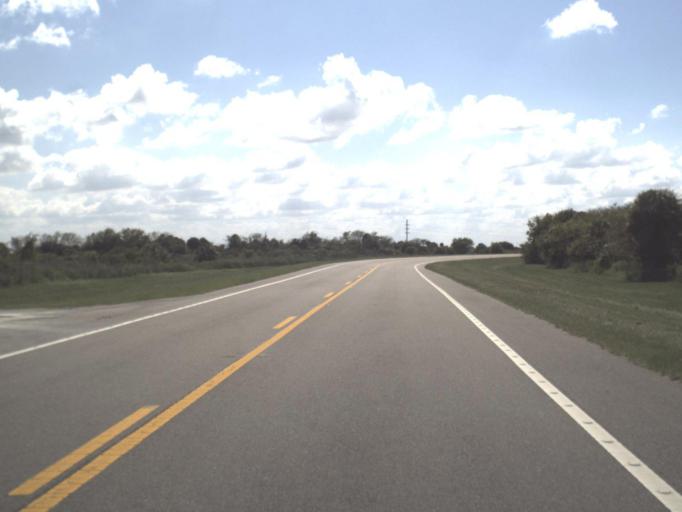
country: US
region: Florida
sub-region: Glades County
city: Moore Haven
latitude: 26.8153
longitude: -81.2029
